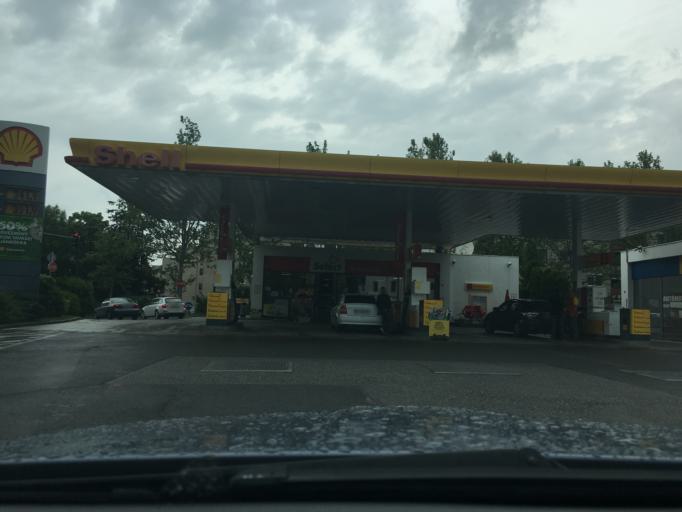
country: HU
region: Hajdu-Bihar
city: Debrecen
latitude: 47.5351
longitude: 21.6124
